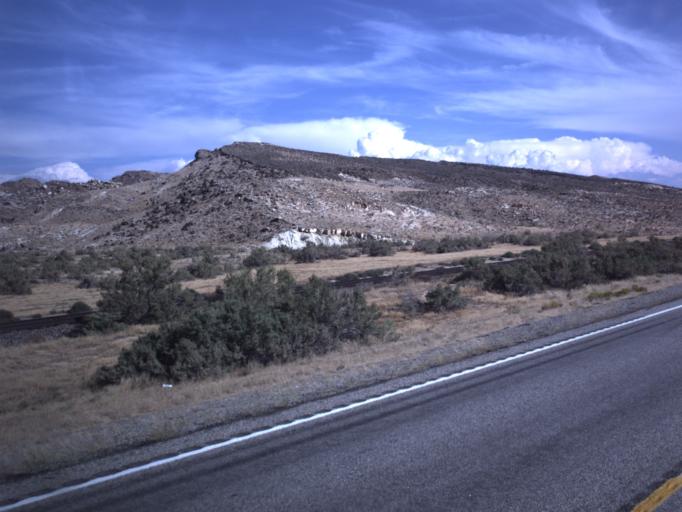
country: US
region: Utah
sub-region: Grand County
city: Moab
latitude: 38.8663
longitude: -109.8090
